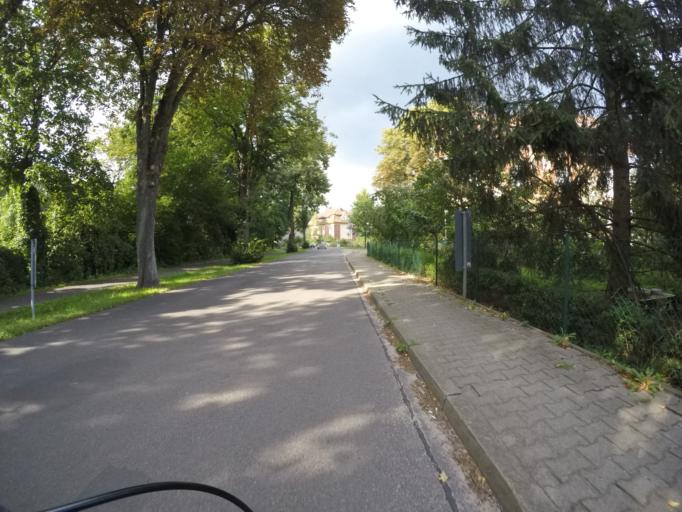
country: DE
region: Brandenburg
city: Werder
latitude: 52.3496
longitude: 12.9831
